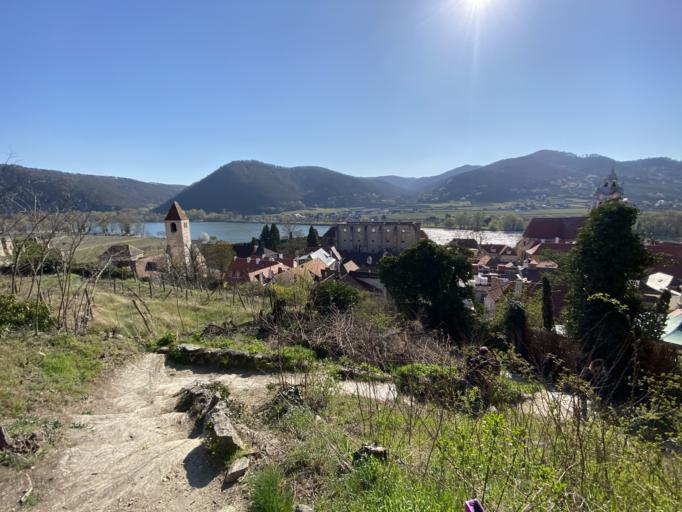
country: AT
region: Lower Austria
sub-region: Politischer Bezirk Krems
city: Durnstein
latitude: 48.3954
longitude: 15.5213
